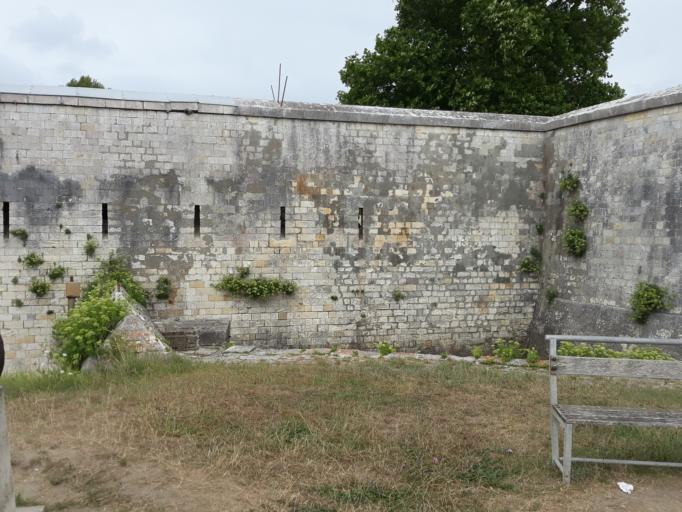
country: FR
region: Poitou-Charentes
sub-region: Departement de la Charente-Maritime
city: Boyard-Ville
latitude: 46.0099
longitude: -1.1749
